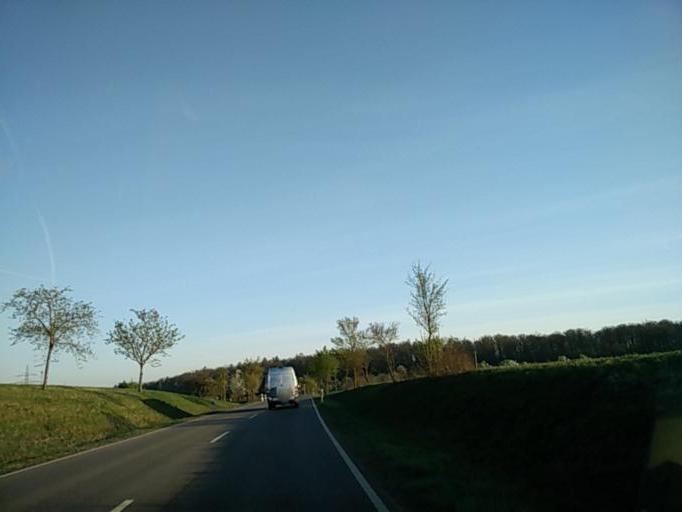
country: DE
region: Baden-Wuerttemberg
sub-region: Regierungsbezirk Stuttgart
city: Hildrizhausen
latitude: 48.6308
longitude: 8.9576
